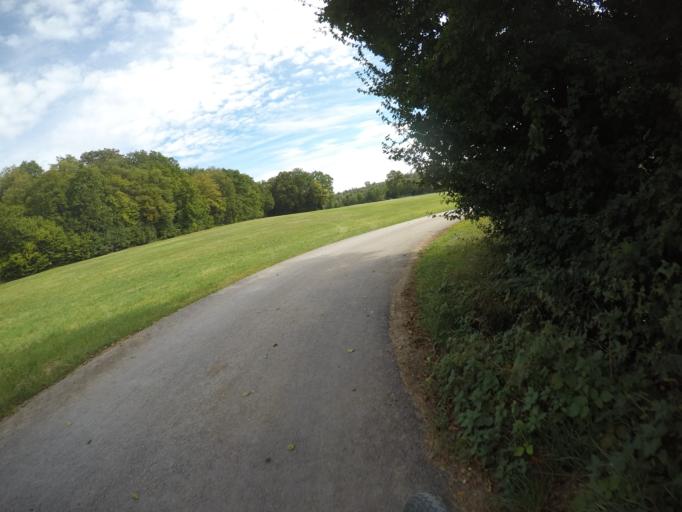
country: DE
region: Baden-Wuerttemberg
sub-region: Karlsruhe Region
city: Muhlacker
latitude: 48.9715
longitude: 8.8758
